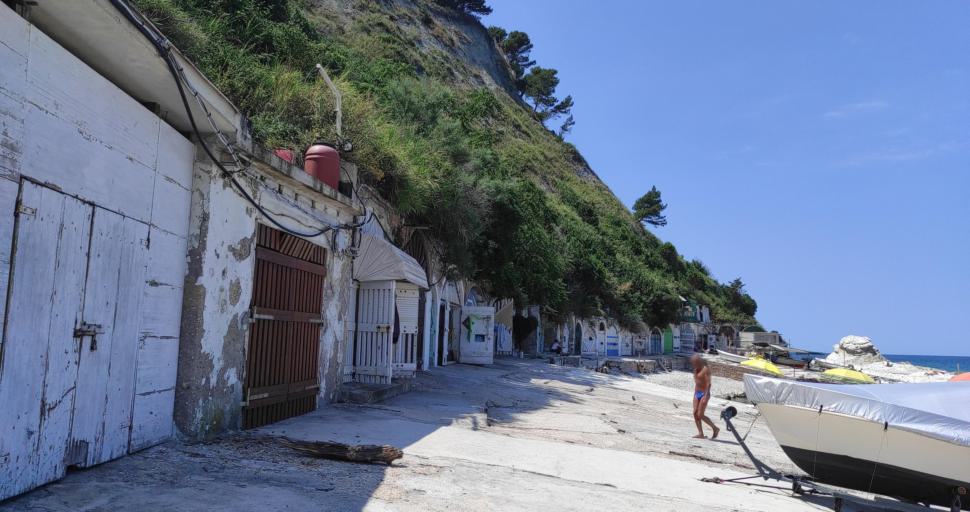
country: IT
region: The Marches
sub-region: Provincia di Ancona
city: Pietra la Croce
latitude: 43.6182
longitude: 13.5320
